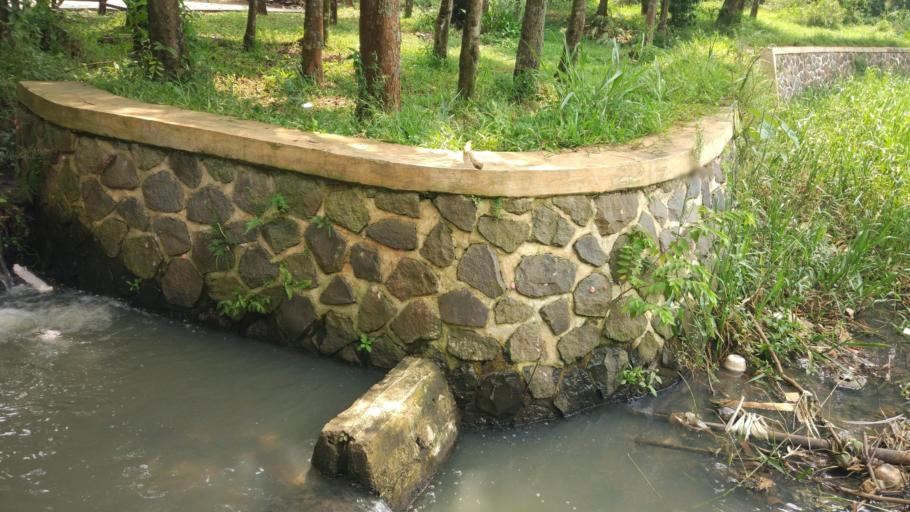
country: ID
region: West Java
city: Ciampea
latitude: -6.5818
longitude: 106.7337
